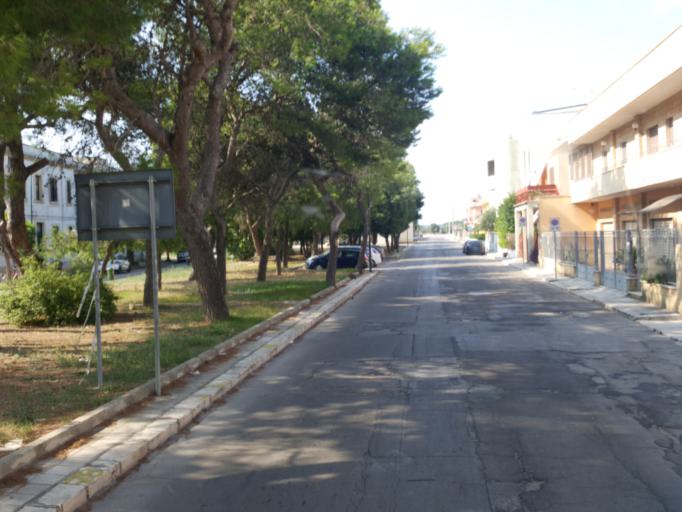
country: IT
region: Apulia
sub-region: Provincia di Lecce
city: Campi Salentina
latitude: 40.4031
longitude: 18.0211
